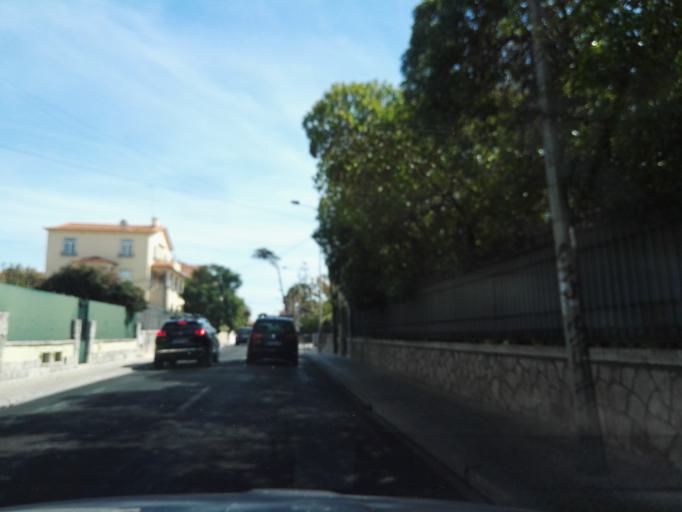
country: PT
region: Lisbon
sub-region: Cascais
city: Estoril
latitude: 38.7017
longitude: -9.3901
